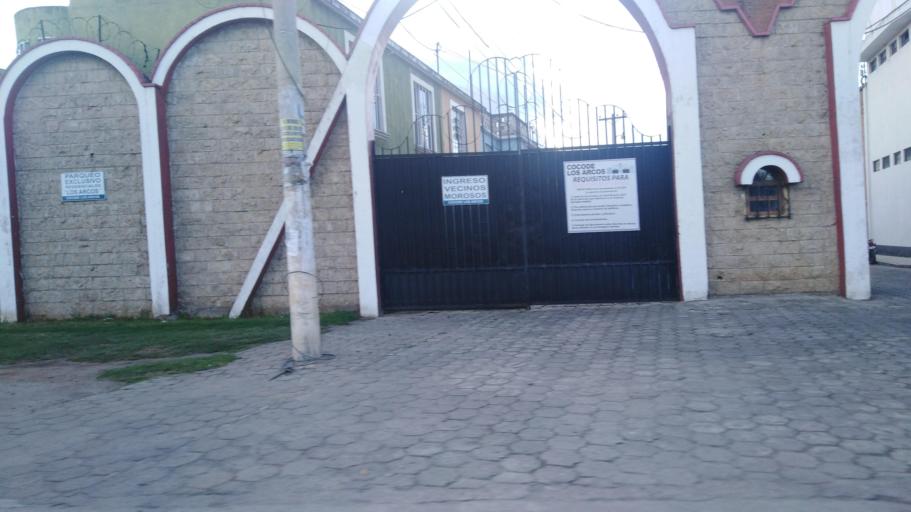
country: GT
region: Quetzaltenango
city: Olintepeque
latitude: 14.8641
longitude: -91.5125
